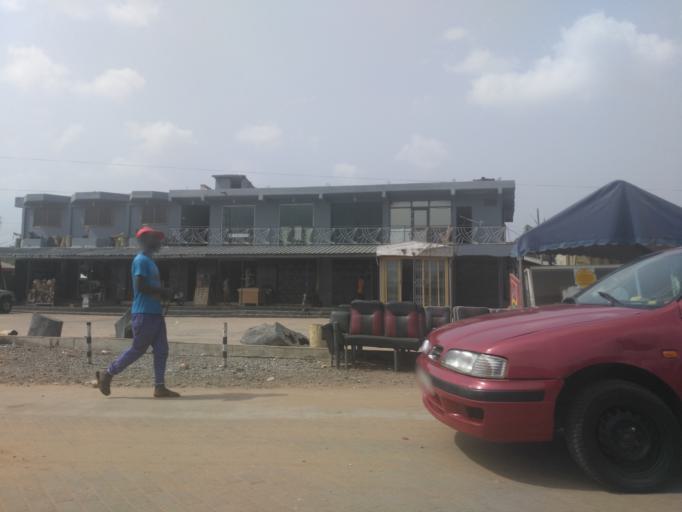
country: GH
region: Greater Accra
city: Dome
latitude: 5.6103
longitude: -0.2277
